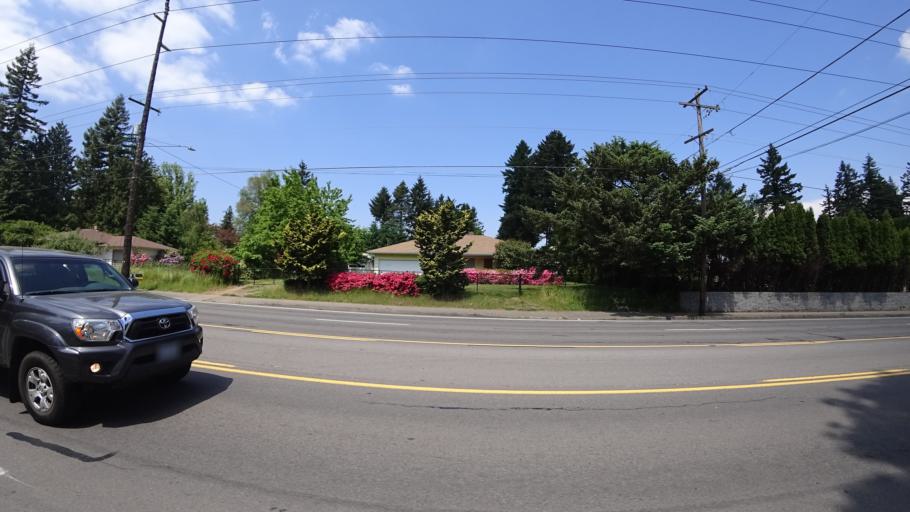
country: US
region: Oregon
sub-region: Multnomah County
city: Fairview
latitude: 45.5264
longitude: -122.4915
